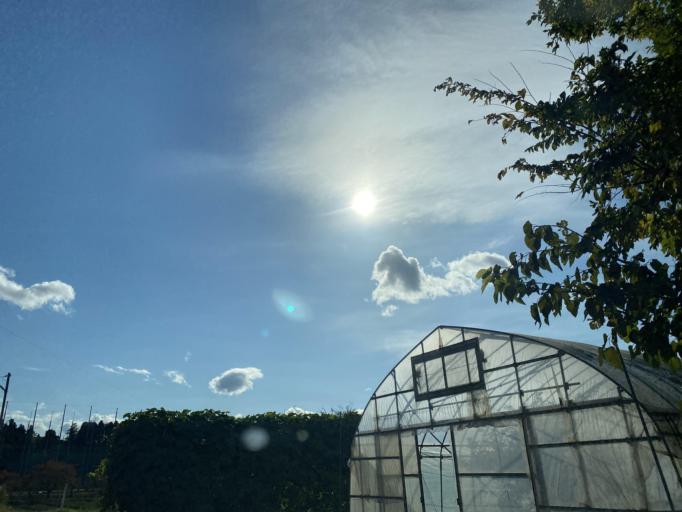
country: JP
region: Fukushima
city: Koriyama
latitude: 37.3612
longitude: 140.3339
